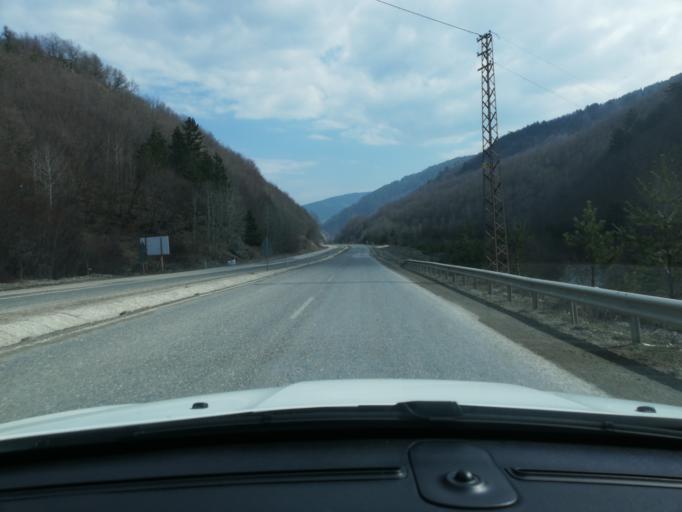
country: TR
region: Kastamonu
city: Kuzyaka
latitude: 41.1148
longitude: 33.7501
